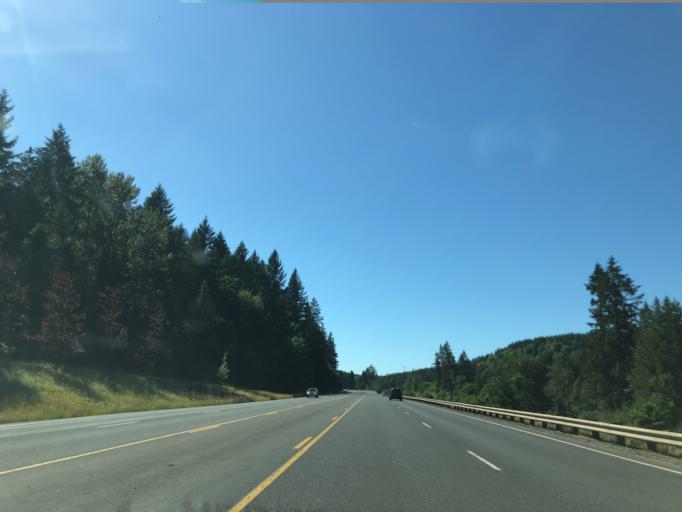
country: US
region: Oregon
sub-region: Linn County
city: Sweet Home
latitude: 44.4020
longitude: -122.7458
